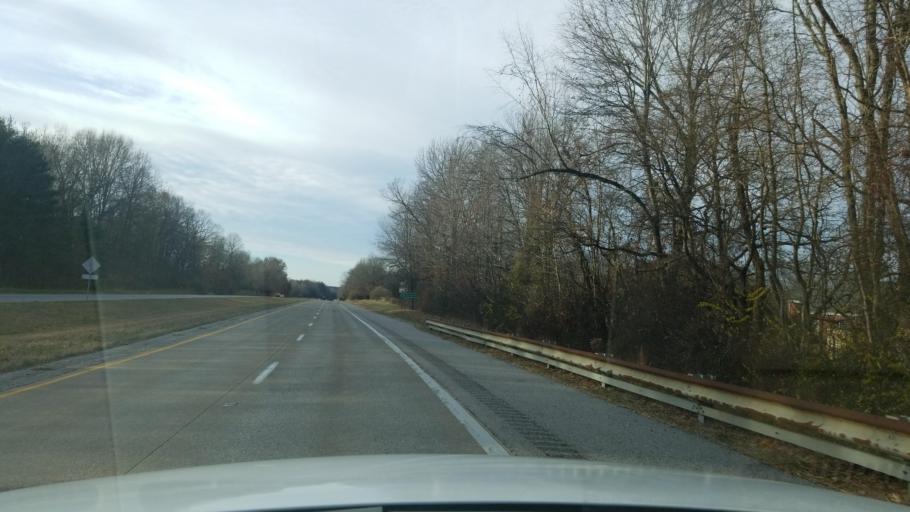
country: US
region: Indiana
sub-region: Vanderburgh County
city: Evansville
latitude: 37.9630
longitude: -87.6896
